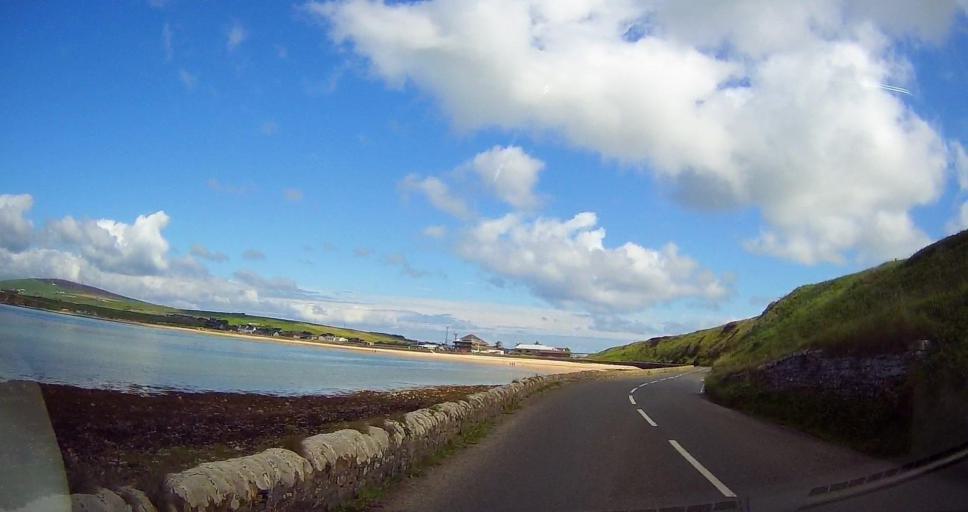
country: GB
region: Scotland
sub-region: Orkney Islands
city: Orkney
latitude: 58.9569
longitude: -2.9697
